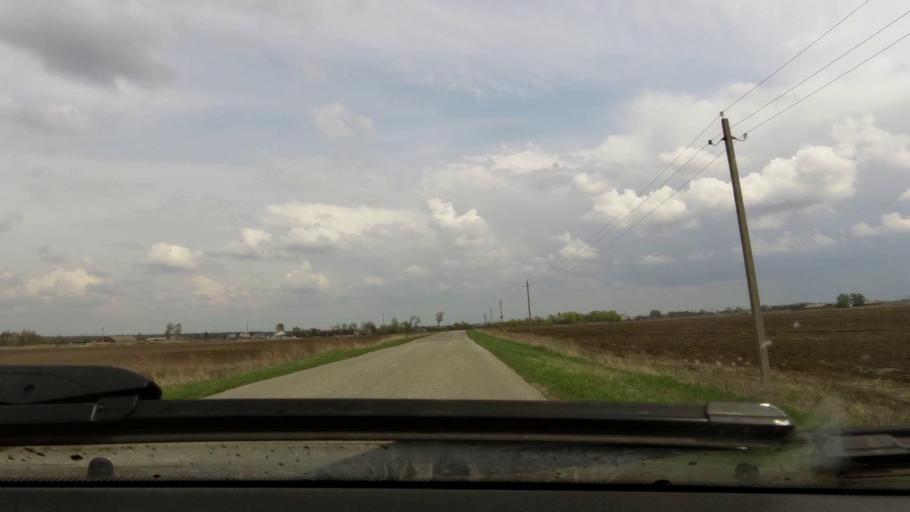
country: RU
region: Rjazan
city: Bagramovo
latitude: 54.7487
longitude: 39.4148
